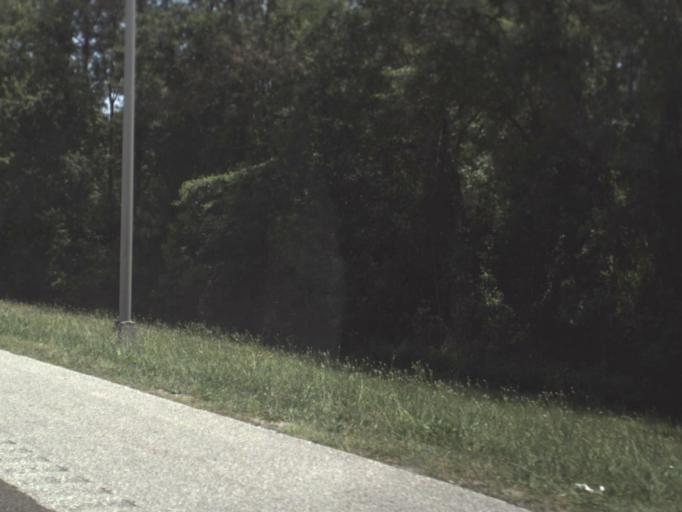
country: US
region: Florida
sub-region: Saint Johns County
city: Fruit Cove
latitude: 30.1704
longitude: -81.6091
